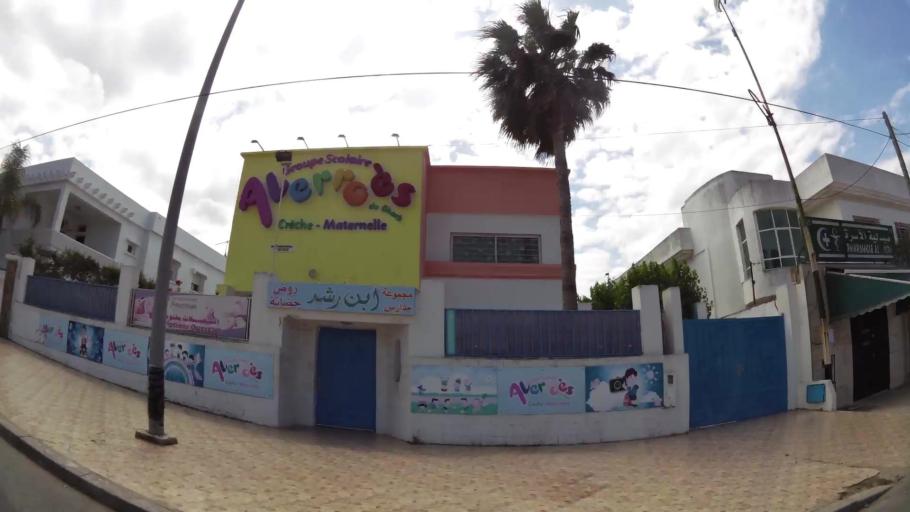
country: MA
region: Gharb-Chrarda-Beni Hssen
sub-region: Kenitra Province
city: Kenitra
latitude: 34.2582
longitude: -6.6030
